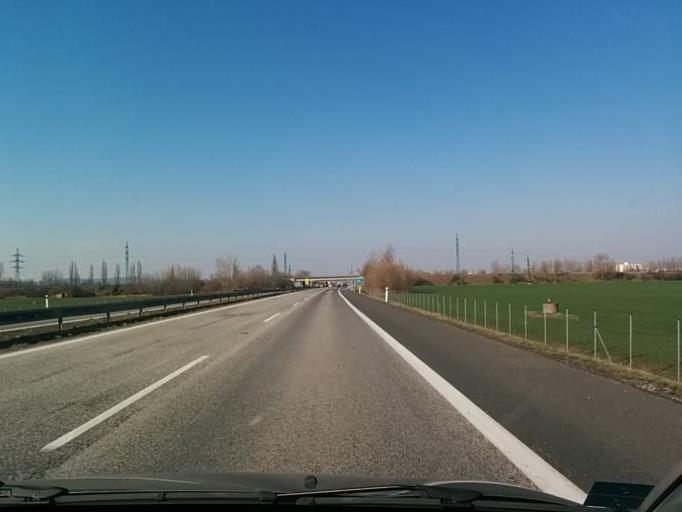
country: SK
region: Trnavsky
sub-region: Okres Trnava
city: Piestany
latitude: 48.5844
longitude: 17.7897
